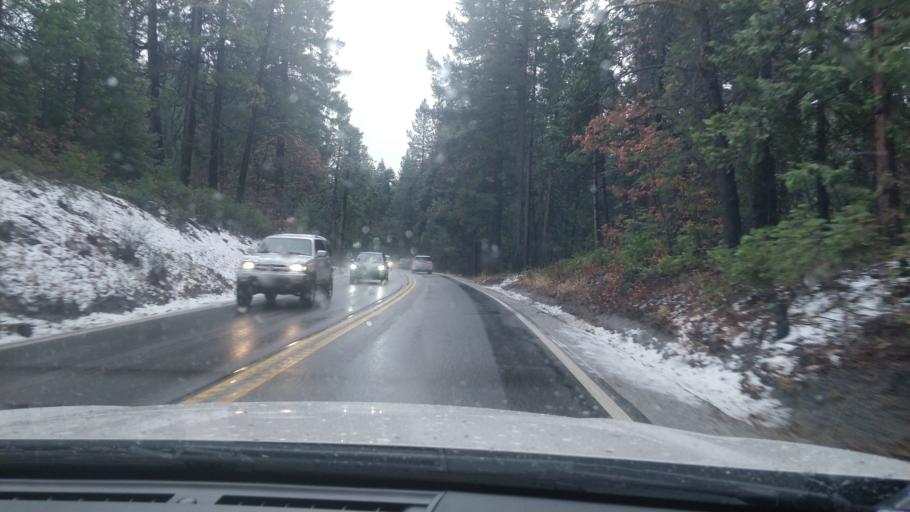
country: US
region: California
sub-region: Nevada County
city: Nevada City
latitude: 39.3144
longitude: -120.7818
